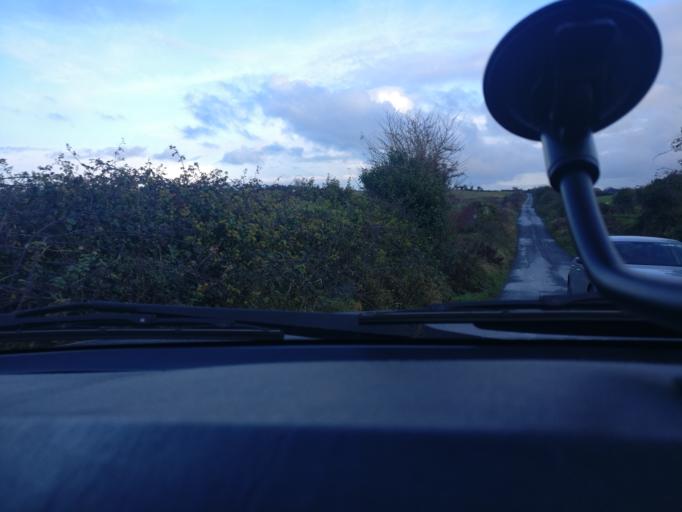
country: IE
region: Connaught
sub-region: County Galway
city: Athenry
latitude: 53.1980
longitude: -8.6959
